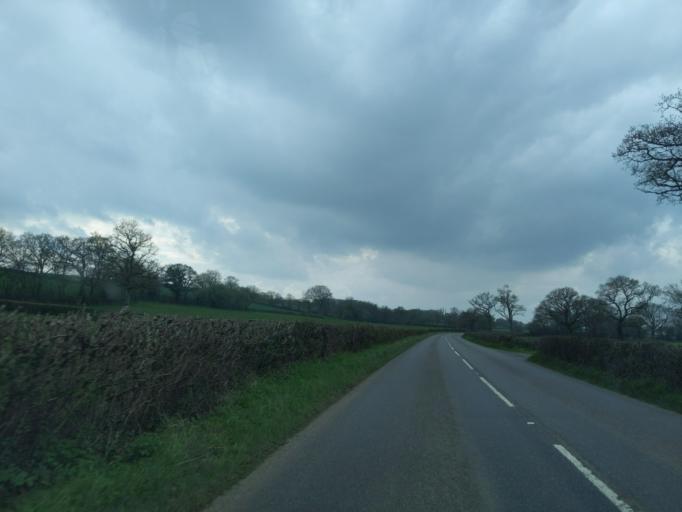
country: GB
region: England
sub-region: Devon
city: Winkleigh
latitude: 50.8459
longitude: -3.8481
